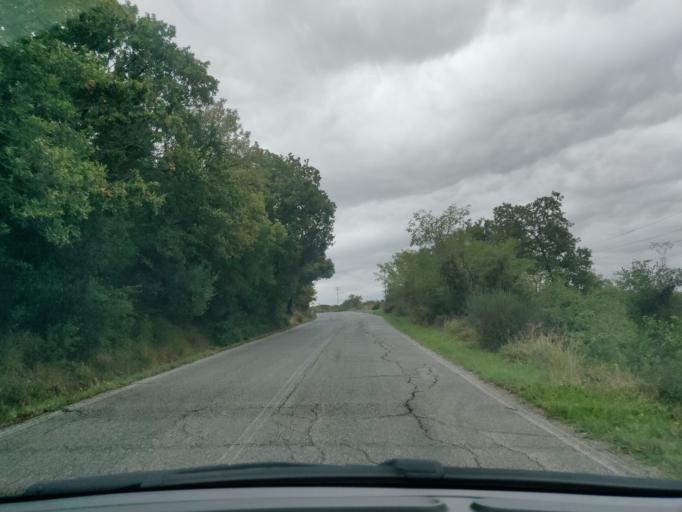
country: IT
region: Latium
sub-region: Citta metropolitana di Roma Capitale
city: Allumiere
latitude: 42.1258
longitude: 11.8595
